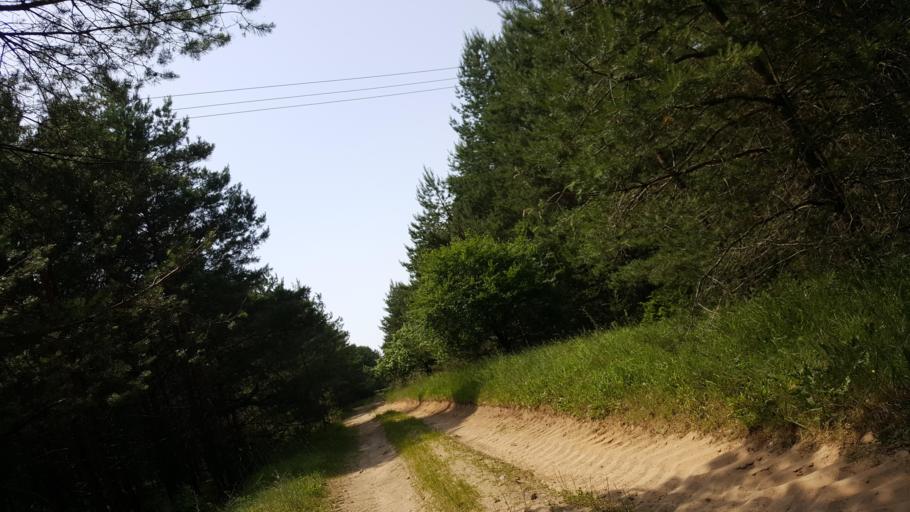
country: BY
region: Brest
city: Kamyanyuki
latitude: 52.5176
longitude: 23.8486
